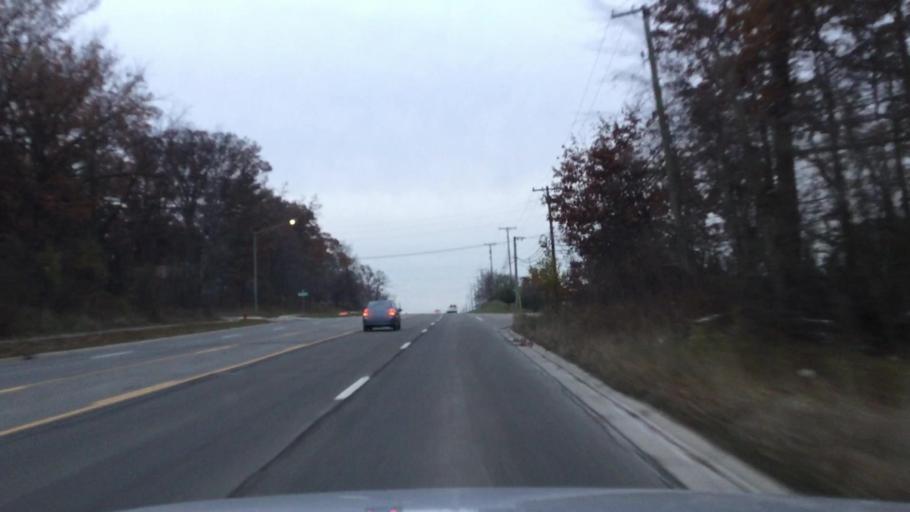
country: US
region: Michigan
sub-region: Oakland County
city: Pontiac
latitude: 42.6305
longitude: -83.2494
